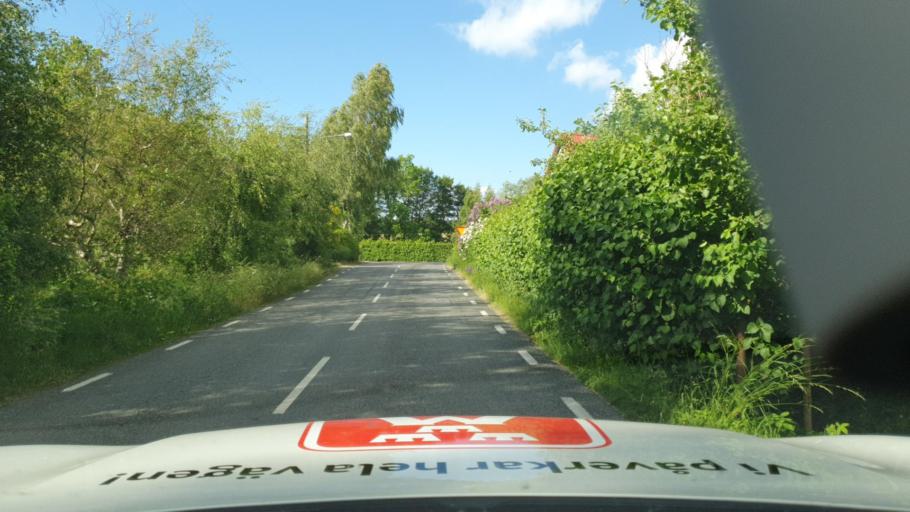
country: SE
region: Skane
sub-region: Simrishamns Kommun
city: Kivik
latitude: 55.6252
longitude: 14.2516
